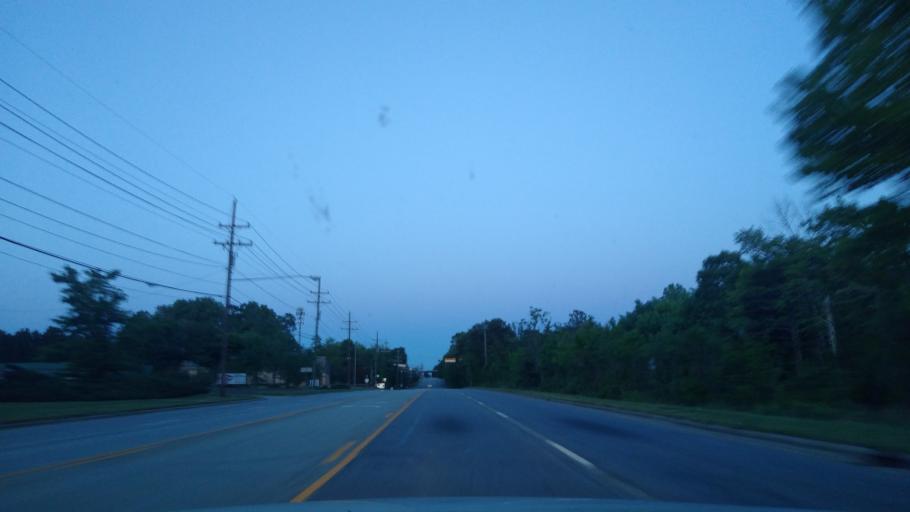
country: US
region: North Carolina
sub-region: Guilford County
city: Oak Ridge
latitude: 36.0935
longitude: -79.9628
